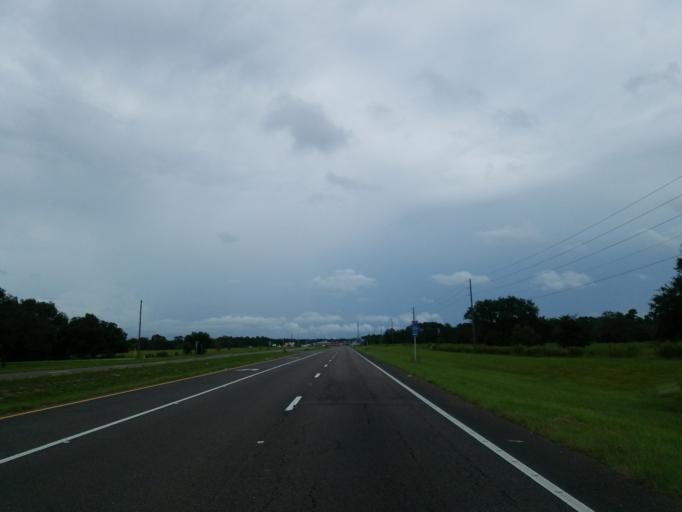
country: US
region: Florida
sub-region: Sumter County
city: Wildwood
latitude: 28.8774
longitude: -82.1088
